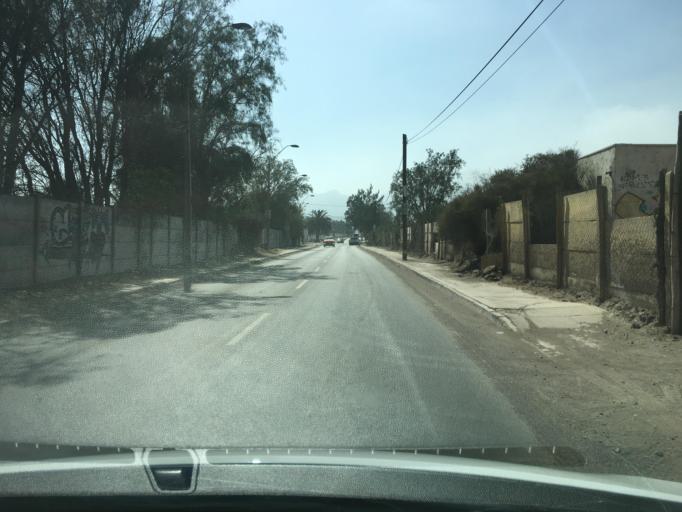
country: CL
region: Atacama
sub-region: Provincia de Copiapo
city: Copiapo
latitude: -27.4129
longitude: -70.2838
